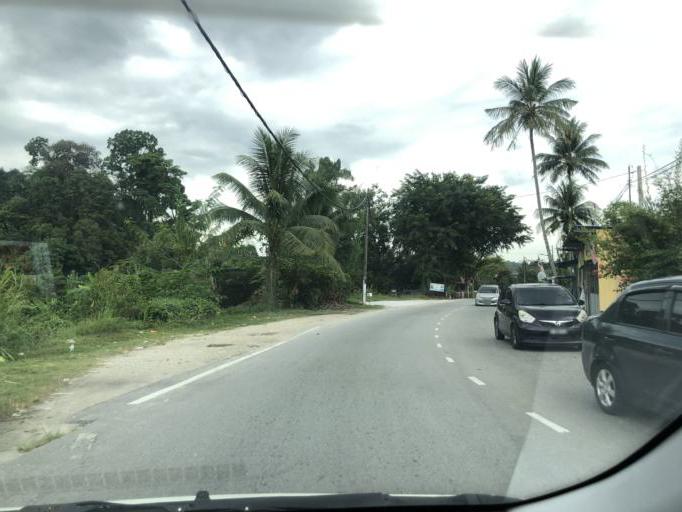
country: MY
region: Putrajaya
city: Putrajaya
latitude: 2.9183
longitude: 101.7588
